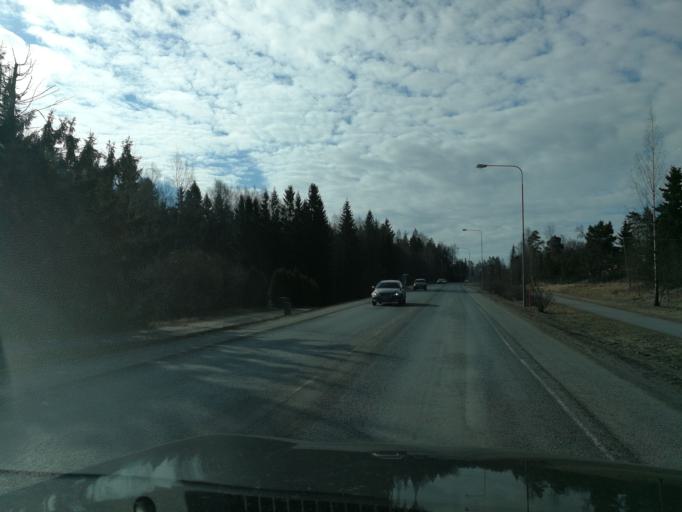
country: FI
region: Uusimaa
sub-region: Helsinki
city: Kirkkonummi
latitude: 60.1142
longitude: 24.4448
